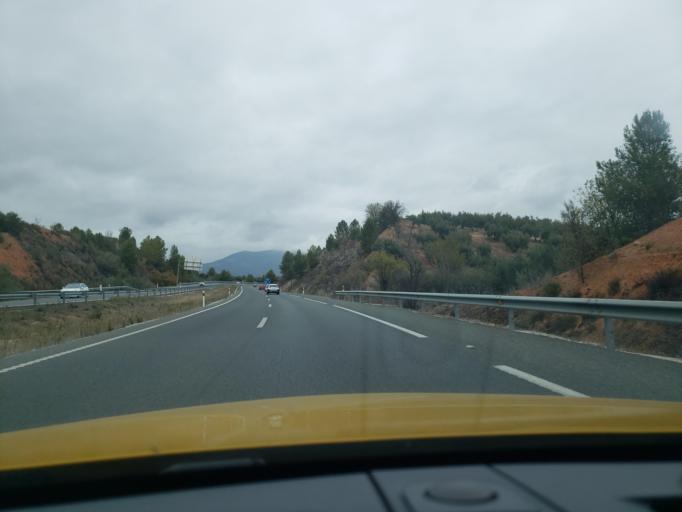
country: ES
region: Andalusia
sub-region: Provincia de Granada
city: Calicasas
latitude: 37.2833
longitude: -3.6575
